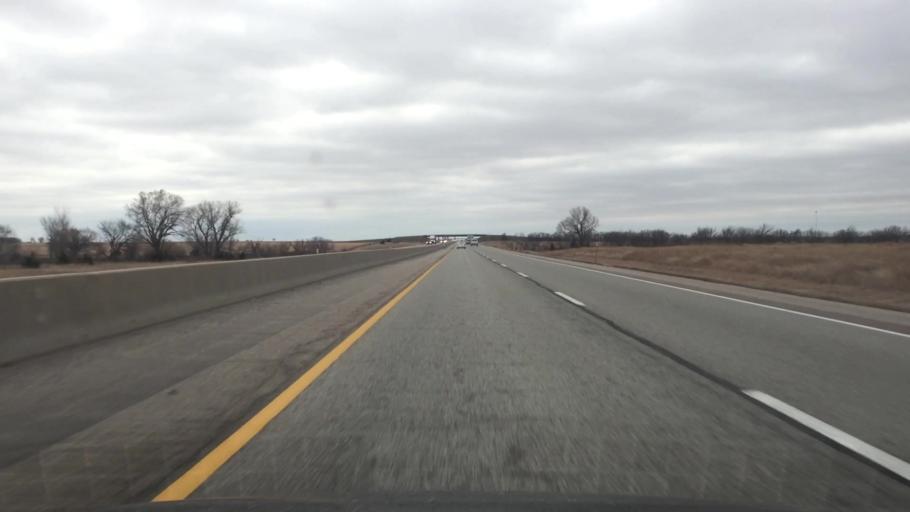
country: US
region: Kansas
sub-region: Butler County
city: El Dorado
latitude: 38.0192
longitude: -96.6702
